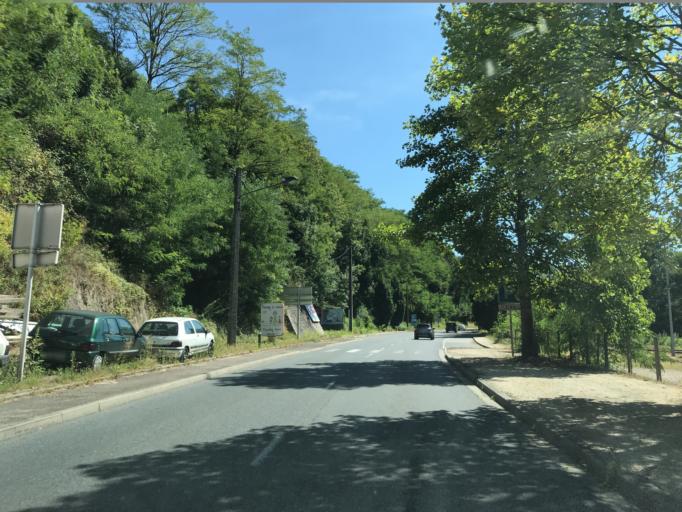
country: FR
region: Limousin
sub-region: Departement de la Correze
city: Cornil
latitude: 45.1821
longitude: 1.6421
